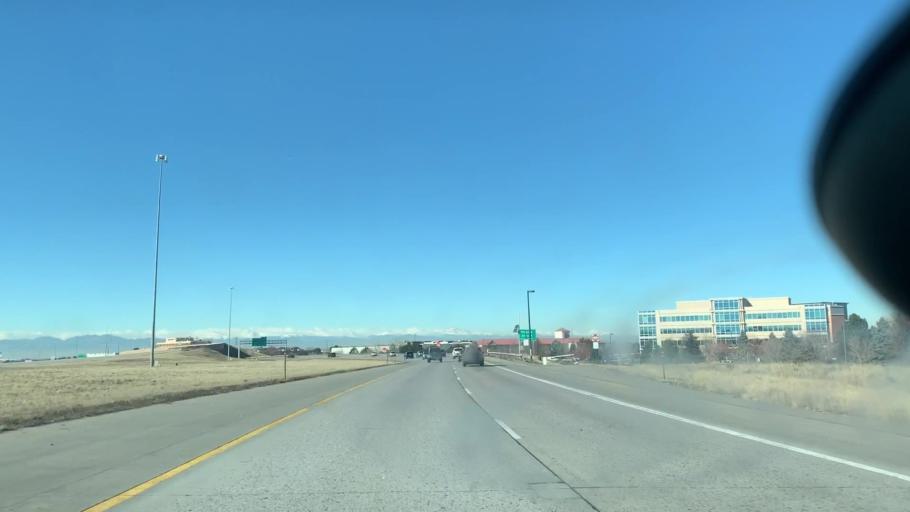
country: US
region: Colorado
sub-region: Adams County
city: Aurora
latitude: 39.7692
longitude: -104.7987
